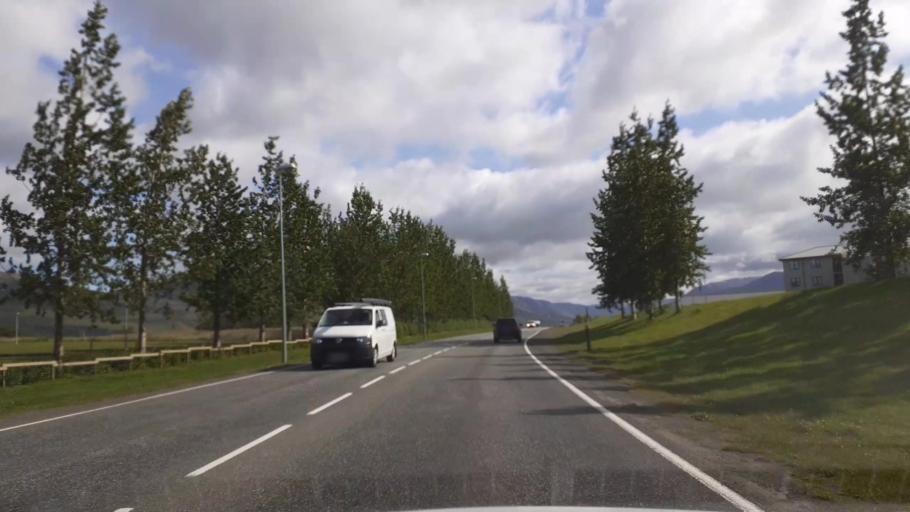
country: IS
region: Northeast
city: Akureyri
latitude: 65.6671
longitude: -18.0943
